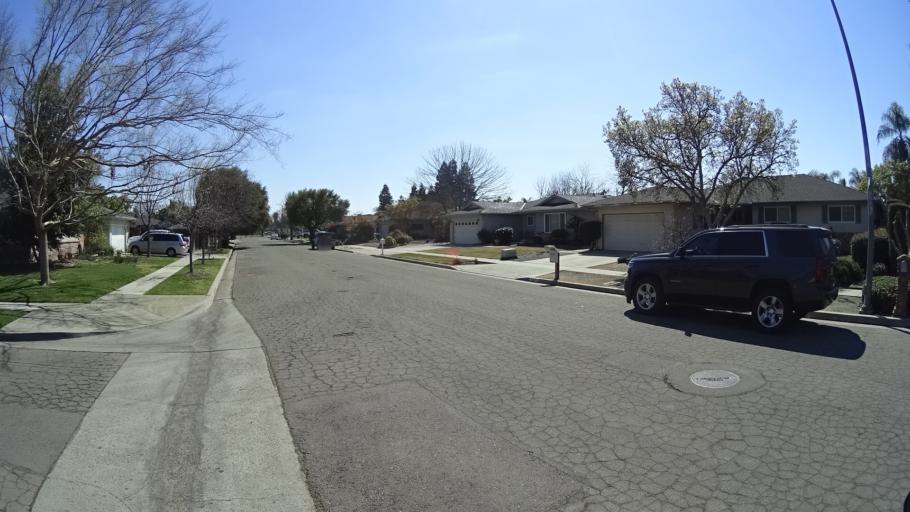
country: US
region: California
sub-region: Fresno County
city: Clovis
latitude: 36.8324
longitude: -119.7383
